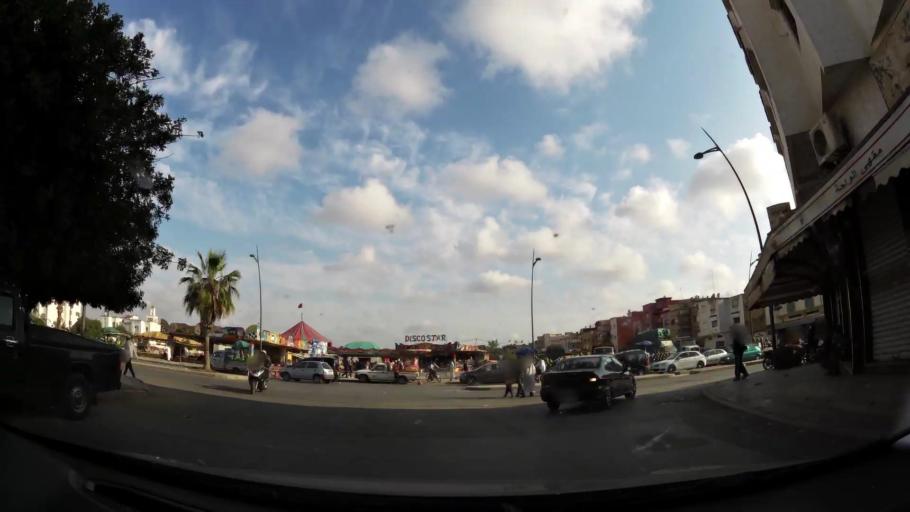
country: MA
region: Rabat-Sale-Zemmour-Zaer
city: Sale
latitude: 34.0471
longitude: -6.7766
